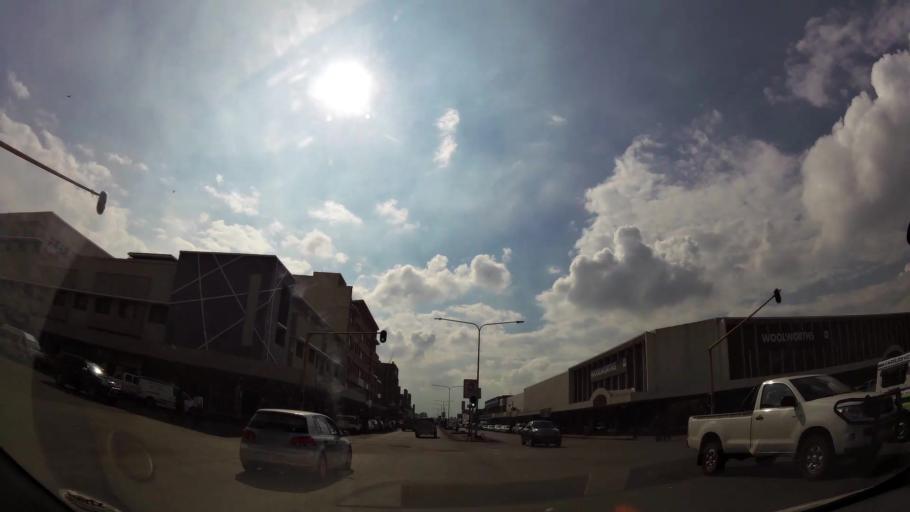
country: ZA
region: Gauteng
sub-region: Sedibeng District Municipality
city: Vereeniging
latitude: -26.6728
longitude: 27.9319
